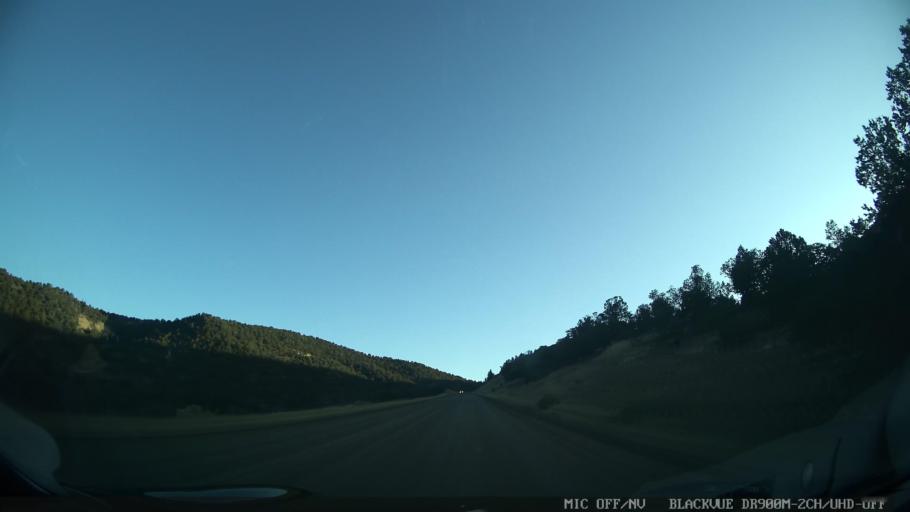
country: US
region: Colorado
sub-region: Grand County
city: Kremmling
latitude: 39.9478
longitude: -106.5280
